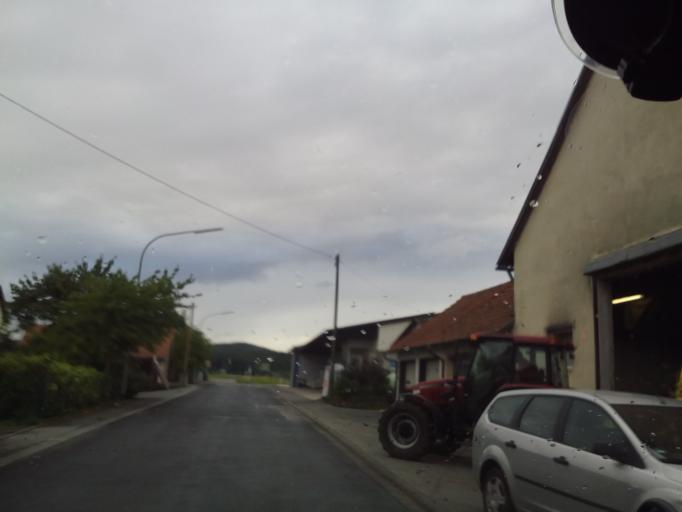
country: DE
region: Bavaria
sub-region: Regierungsbezirk Unterfranken
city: Pfarrweisach
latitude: 50.1924
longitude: 10.7589
